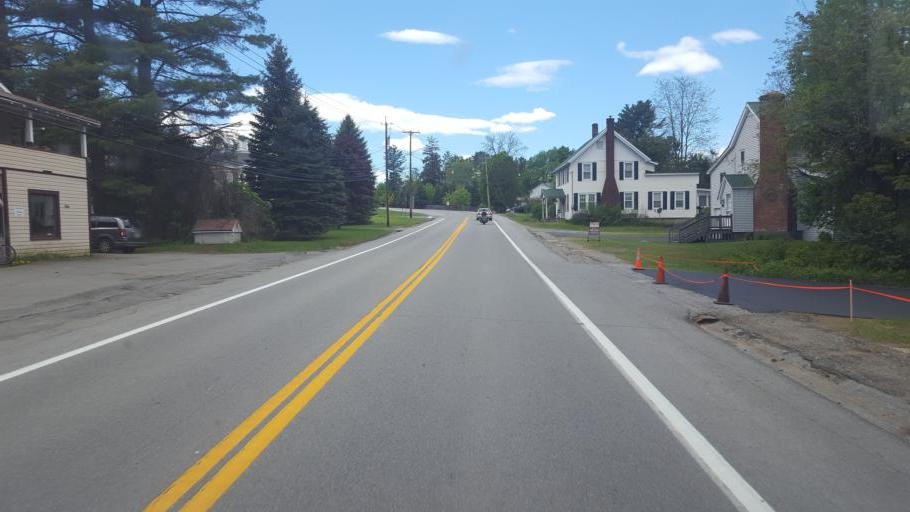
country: US
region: New York
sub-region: Hamilton County
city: Lake Pleasant
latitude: 43.4705
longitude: -74.4099
